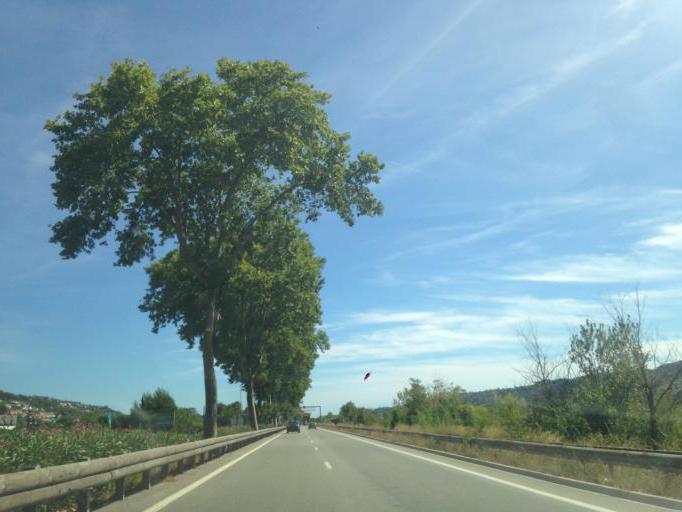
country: FR
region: Provence-Alpes-Cote d'Azur
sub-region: Departement des Alpes-Maritimes
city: Gattieres
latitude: 43.7334
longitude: 7.1845
